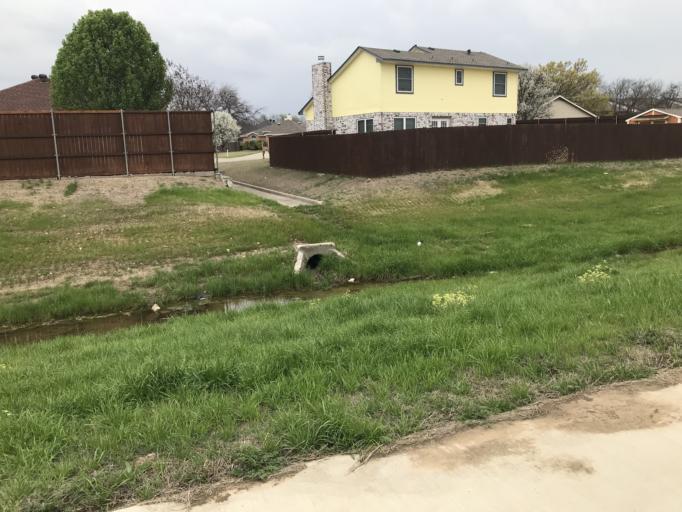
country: US
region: Texas
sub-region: Denton County
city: Denton
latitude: 33.2495
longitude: -97.1362
